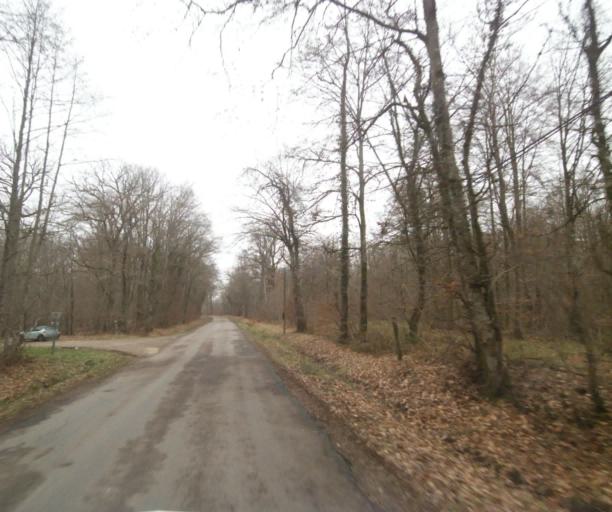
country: FR
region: Champagne-Ardenne
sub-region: Departement de la Haute-Marne
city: Wassy
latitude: 48.5280
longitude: 4.9774
